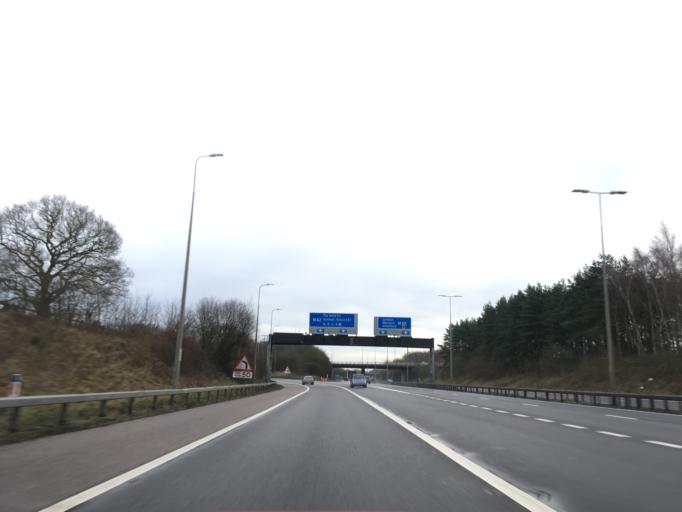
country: GB
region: England
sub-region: Solihull
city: Cheswick Green
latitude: 52.3478
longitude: -1.8164
